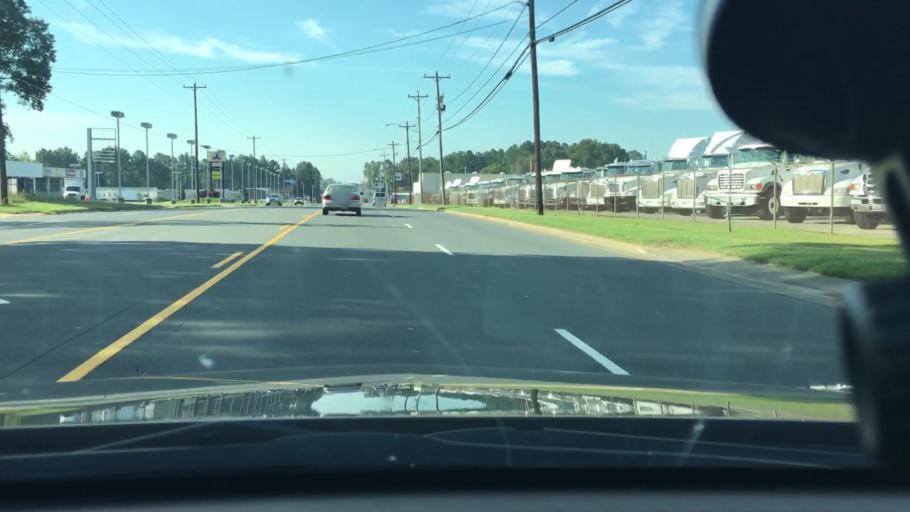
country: US
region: North Carolina
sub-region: Stanly County
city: Albemarle
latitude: 35.3792
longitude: -80.1947
